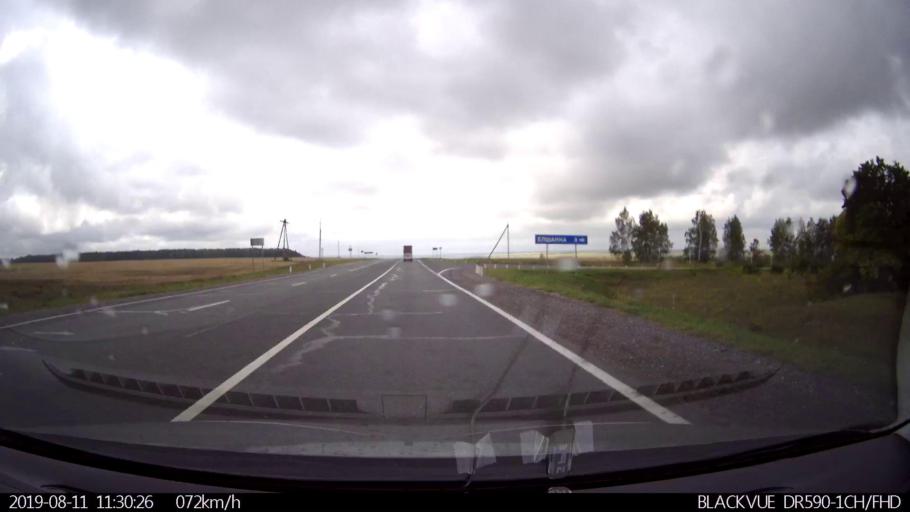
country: RU
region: Ulyanovsk
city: Krasnyy Gulyay
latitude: 54.0586
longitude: 48.2192
